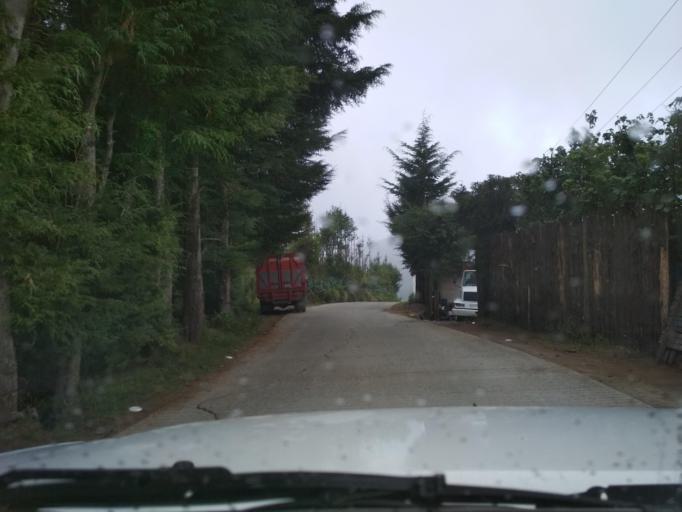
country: MX
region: Veracruz
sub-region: Mariano Escobedo
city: San Isidro el Berro
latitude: 18.9234
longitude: -97.2033
